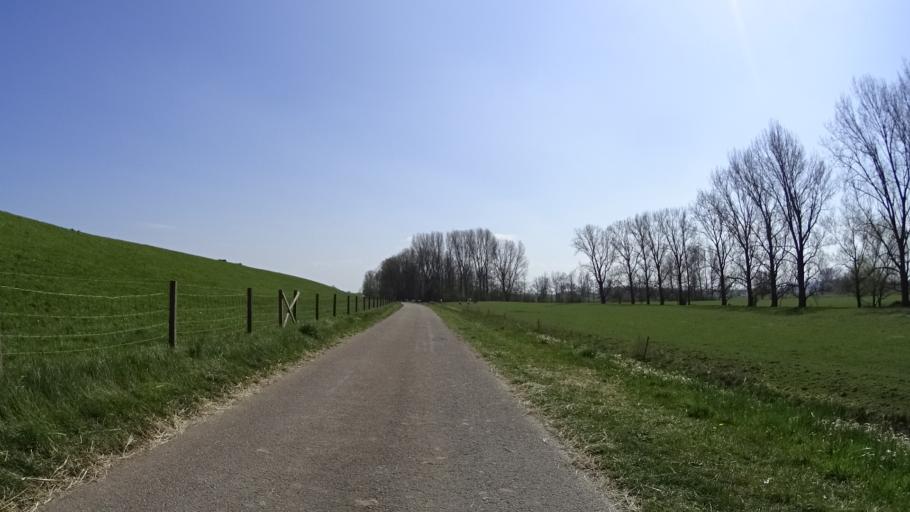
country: DE
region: Lower Saxony
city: Weener
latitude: 53.1286
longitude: 7.3657
